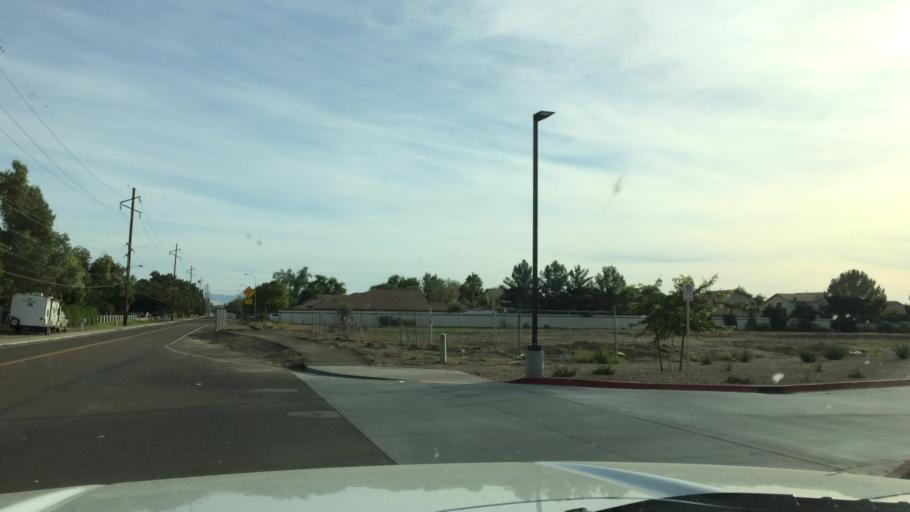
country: US
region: Arizona
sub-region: Maricopa County
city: Peoria
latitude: 33.5653
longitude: -112.2639
